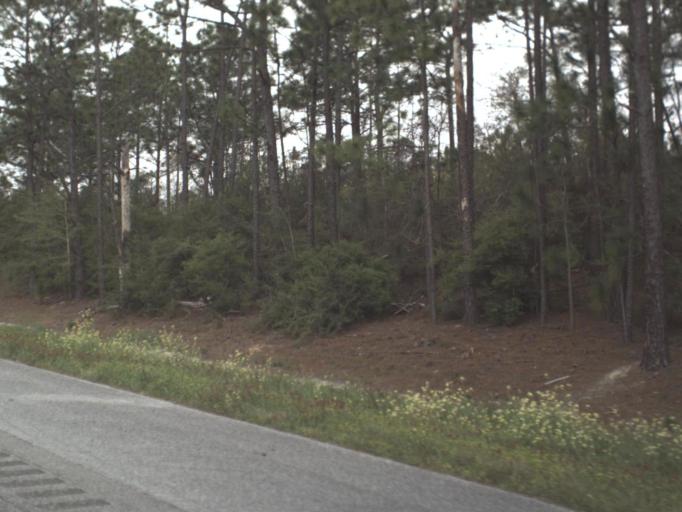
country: US
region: Florida
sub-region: Okaloosa County
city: Crestview
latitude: 30.7258
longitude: -86.4885
